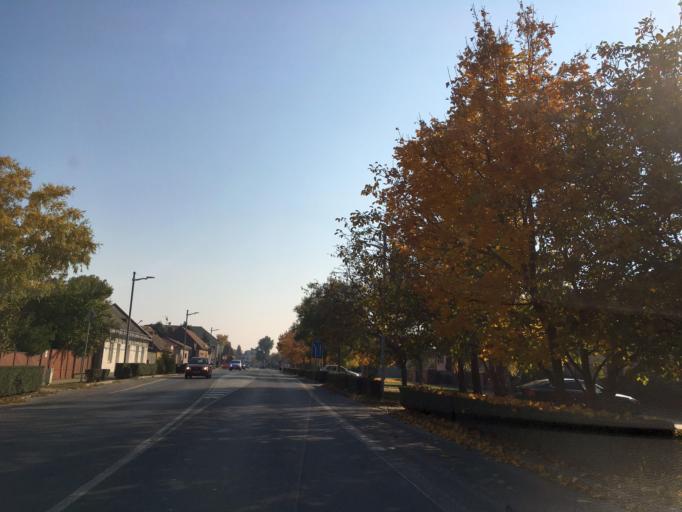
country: SK
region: Bratislavsky
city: Dunajska Luzna
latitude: 48.0990
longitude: 17.2339
